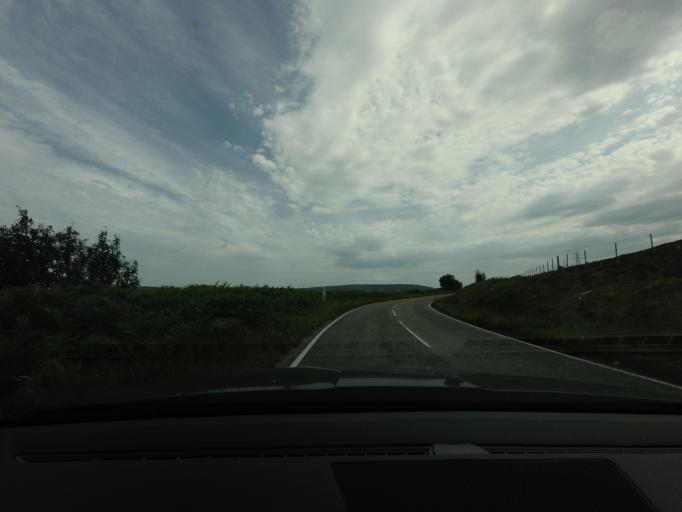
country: GB
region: Scotland
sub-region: Highland
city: Alness
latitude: 57.8219
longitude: -4.2580
